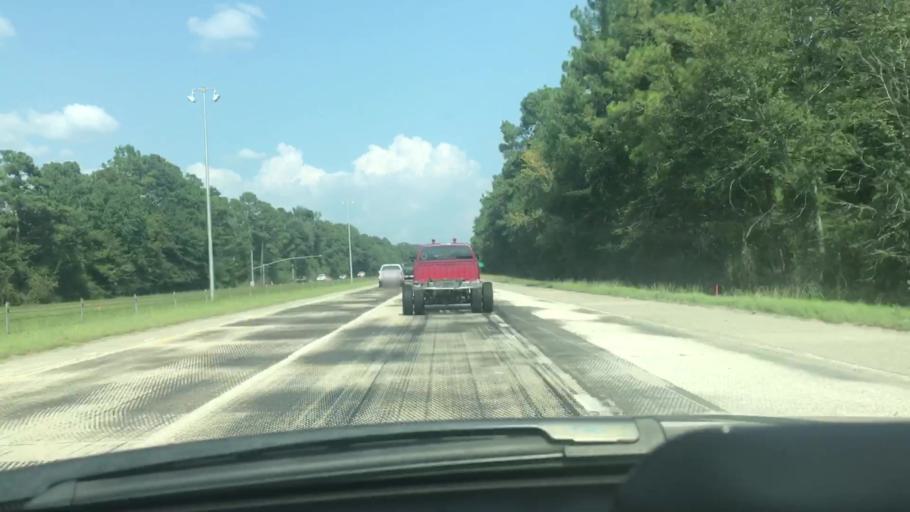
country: US
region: Louisiana
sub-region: Tangipahoa Parish
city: Hammond
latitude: 30.4794
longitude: -90.5148
